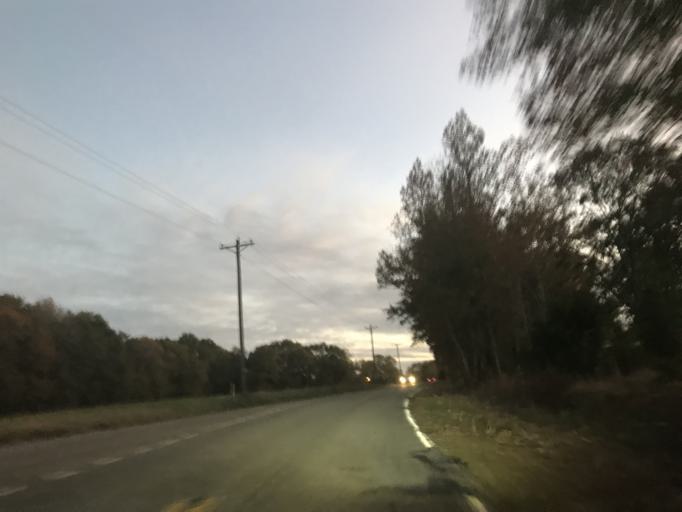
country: US
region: South Carolina
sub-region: Spartanburg County
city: Mayo
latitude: 35.0706
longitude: -81.9000
